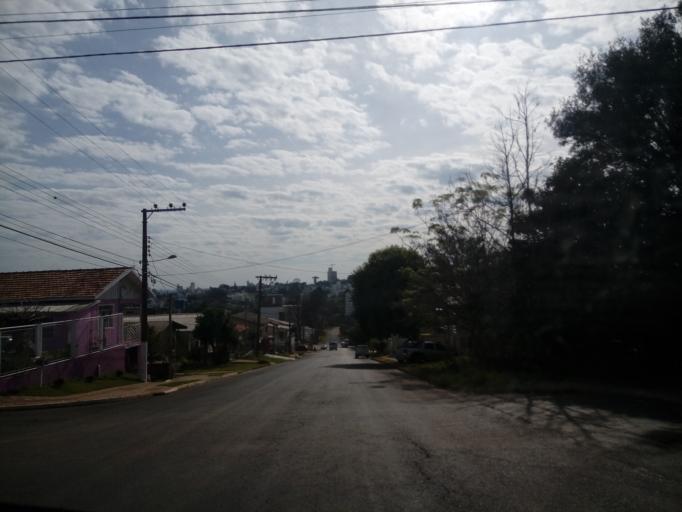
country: BR
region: Santa Catarina
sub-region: Chapeco
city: Chapeco
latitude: -27.1187
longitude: -52.6219
